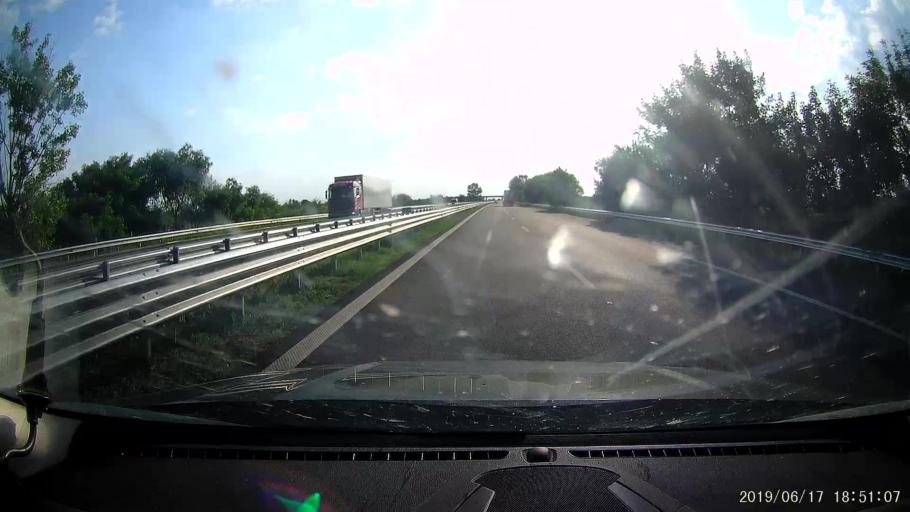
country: BG
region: Plovdiv
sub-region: Obshtina Rakovski
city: Rakovski
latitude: 42.2137
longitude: 24.9808
